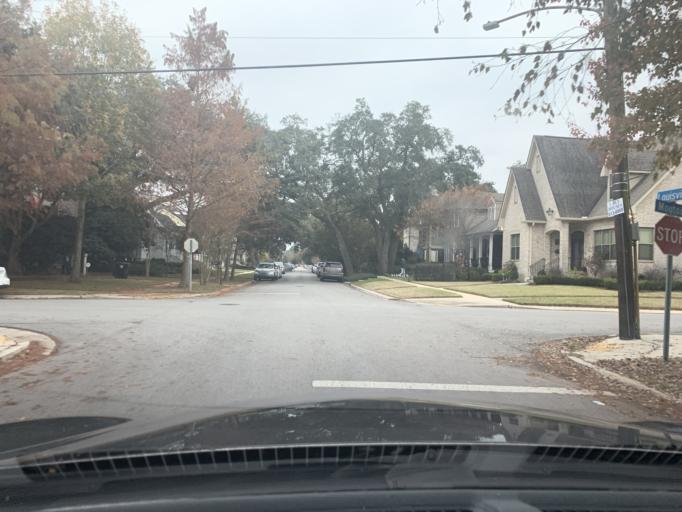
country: US
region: Louisiana
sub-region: Jefferson Parish
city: Metairie
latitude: 30.0162
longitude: -90.1090
